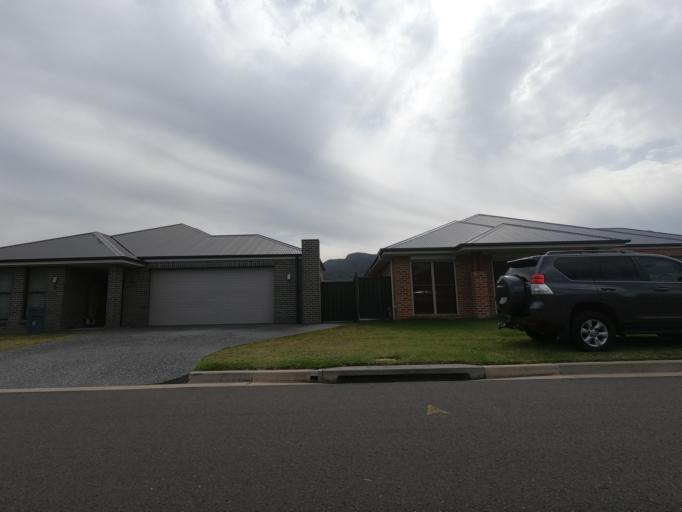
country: AU
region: New South Wales
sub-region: Wollongong
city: Dapto
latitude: -34.4992
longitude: 150.7621
